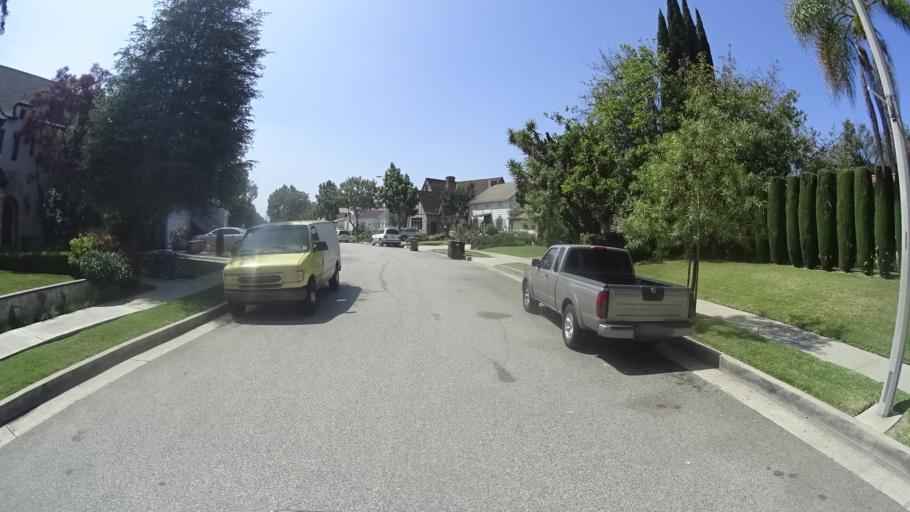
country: US
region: California
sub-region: Los Angeles County
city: View Park-Windsor Hills
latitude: 34.0018
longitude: -118.3381
